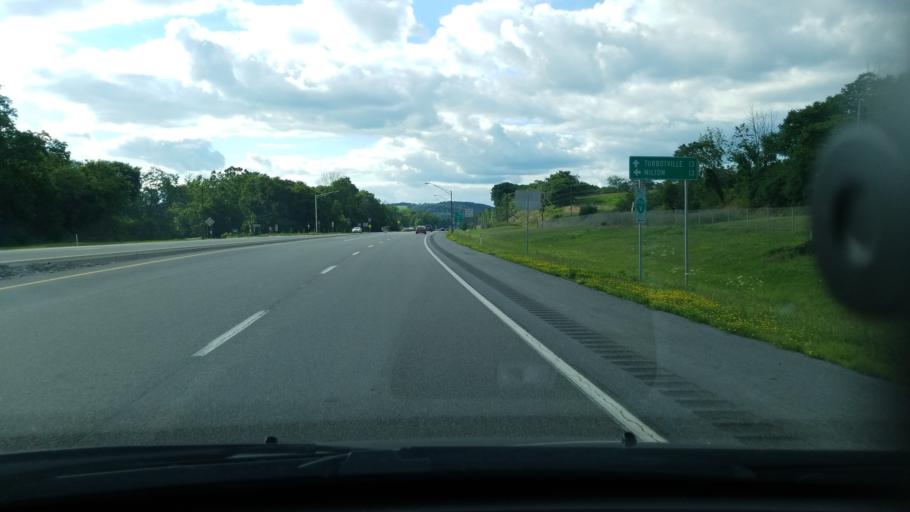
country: US
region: Pennsylvania
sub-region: Montour County
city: Danville
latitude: 40.9850
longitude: -76.6304
